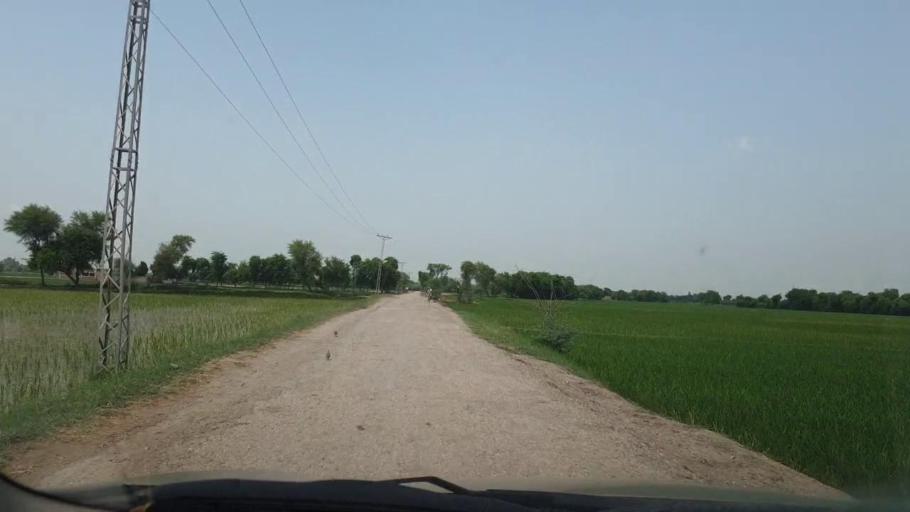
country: PK
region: Sindh
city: Larkana
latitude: 27.5816
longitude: 68.1435
